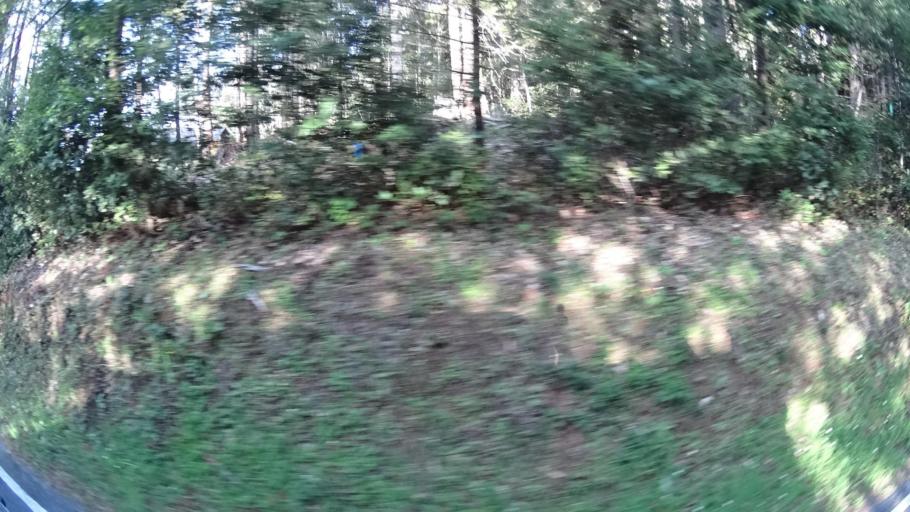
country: US
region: California
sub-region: Humboldt County
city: Bayside
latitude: 40.7553
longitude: -123.9869
